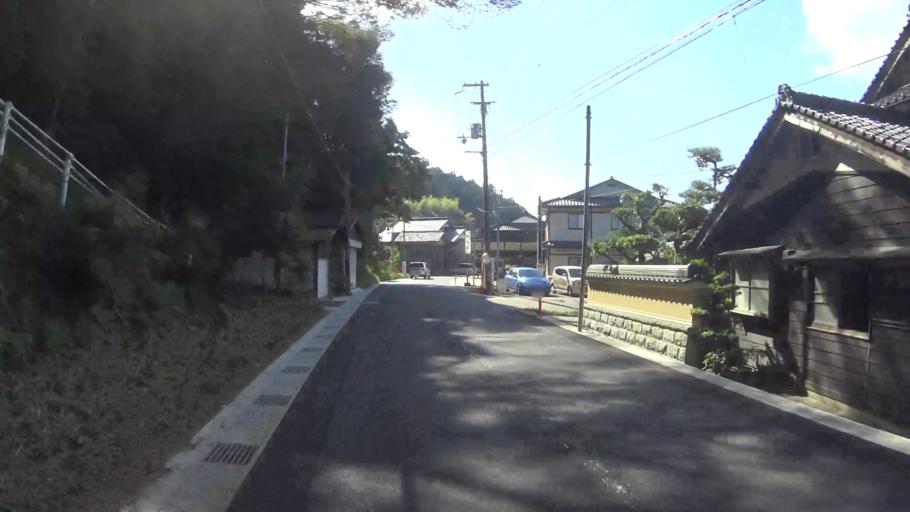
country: JP
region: Kyoto
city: Miyazu
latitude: 35.7089
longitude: 135.1057
